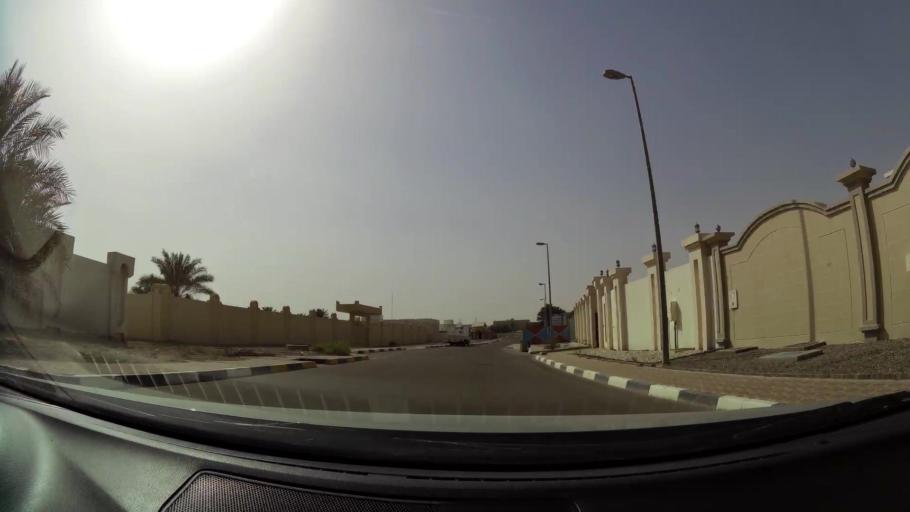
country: AE
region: Abu Dhabi
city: Al Ain
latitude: 24.2483
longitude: 55.6939
